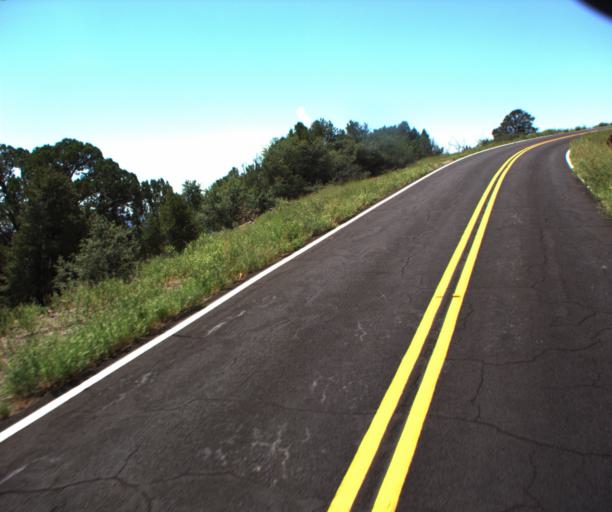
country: US
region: Arizona
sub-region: Greenlee County
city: Morenci
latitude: 33.4288
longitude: -109.3743
